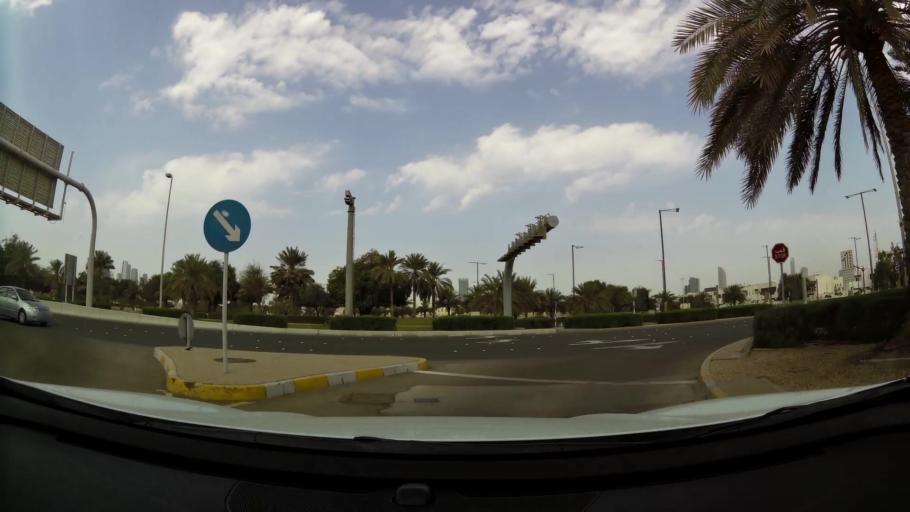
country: AE
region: Abu Dhabi
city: Abu Dhabi
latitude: 24.4531
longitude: 54.3519
